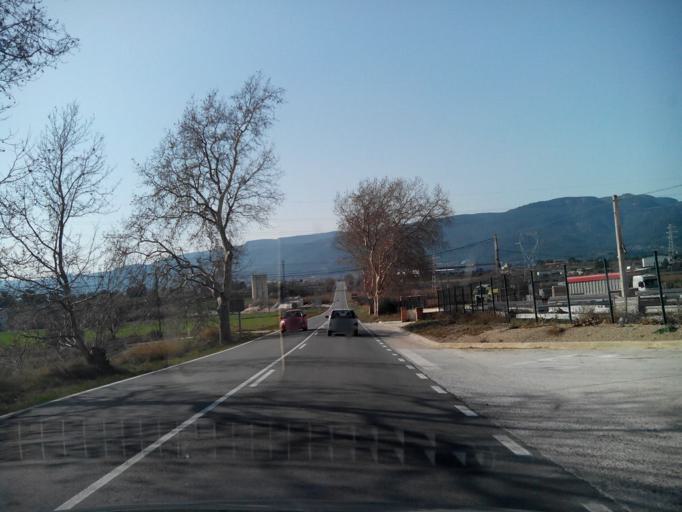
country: ES
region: Catalonia
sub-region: Provincia de Tarragona
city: Montblanc
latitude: 41.3952
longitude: 1.1715
